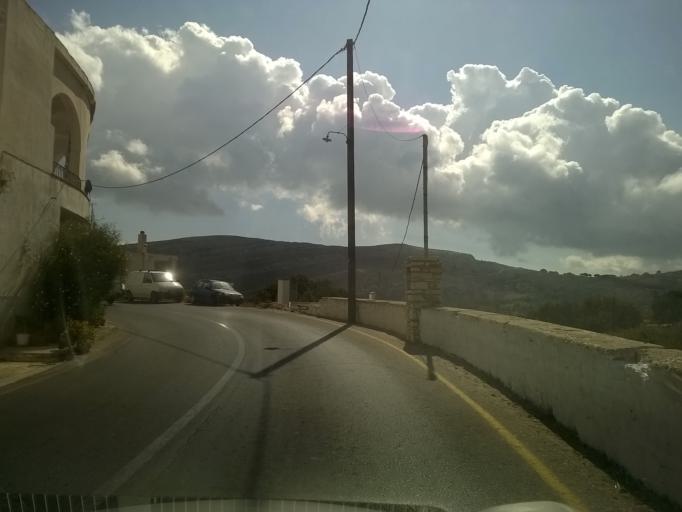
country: GR
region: South Aegean
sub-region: Nomos Kykladon
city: Filotion
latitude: 37.0696
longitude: 25.5191
